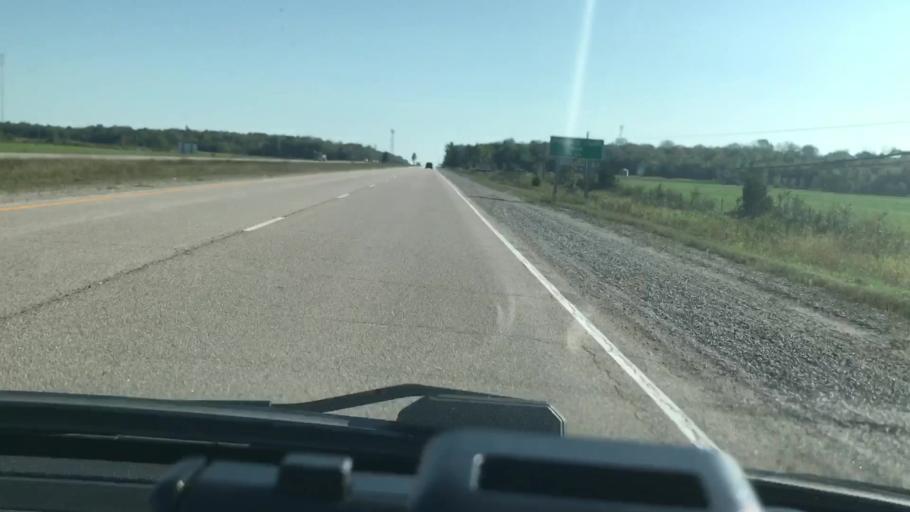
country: CA
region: Ontario
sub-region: Algoma
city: Sault Ste. Marie
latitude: 46.4057
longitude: -84.0679
